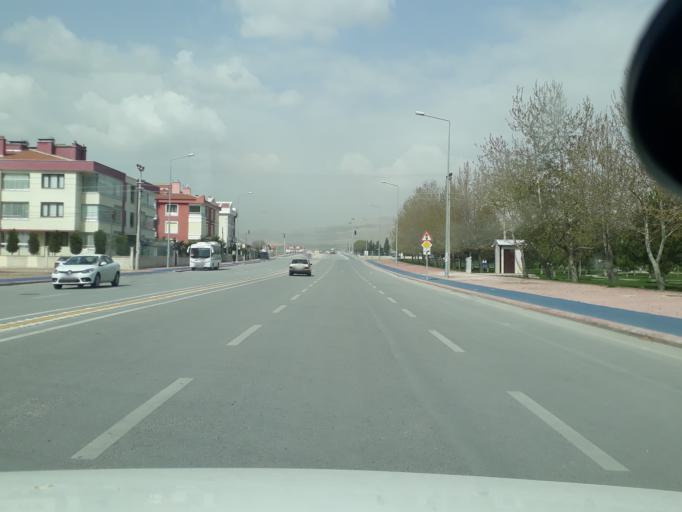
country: TR
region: Konya
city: Selcuklu
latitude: 37.9425
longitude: 32.4920
